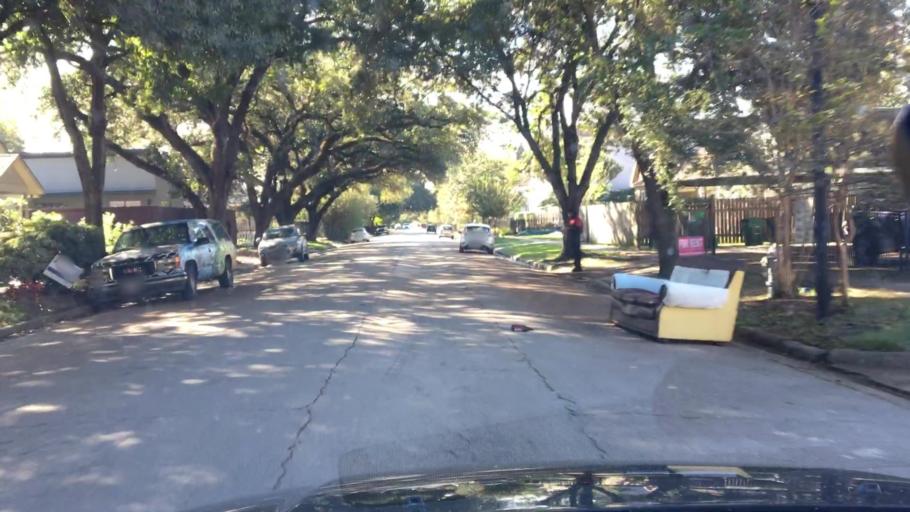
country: US
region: Texas
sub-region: Harris County
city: Houston
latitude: 29.7991
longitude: -95.4014
